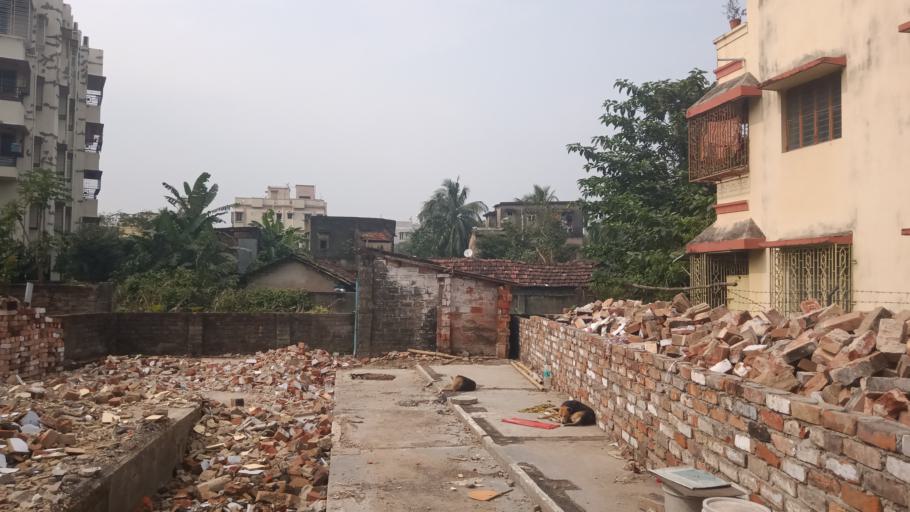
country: IN
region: West Bengal
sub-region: Kolkata
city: Kolkata
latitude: 22.4658
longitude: 88.3844
